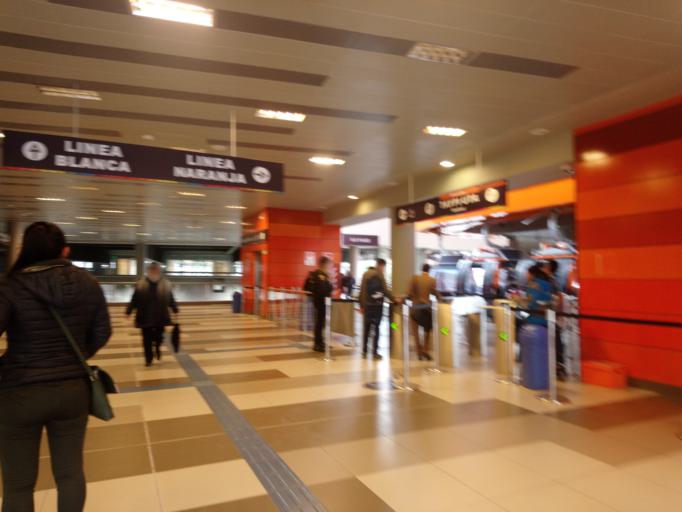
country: BO
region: La Paz
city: La Paz
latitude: -16.4846
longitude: -68.1222
